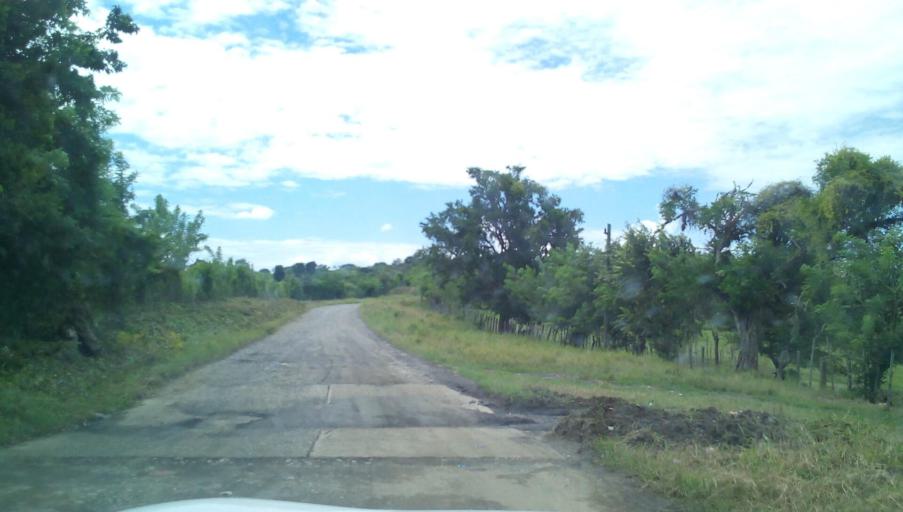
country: MX
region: Veracruz
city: Tepetzintla
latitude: 21.1552
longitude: -97.8530
